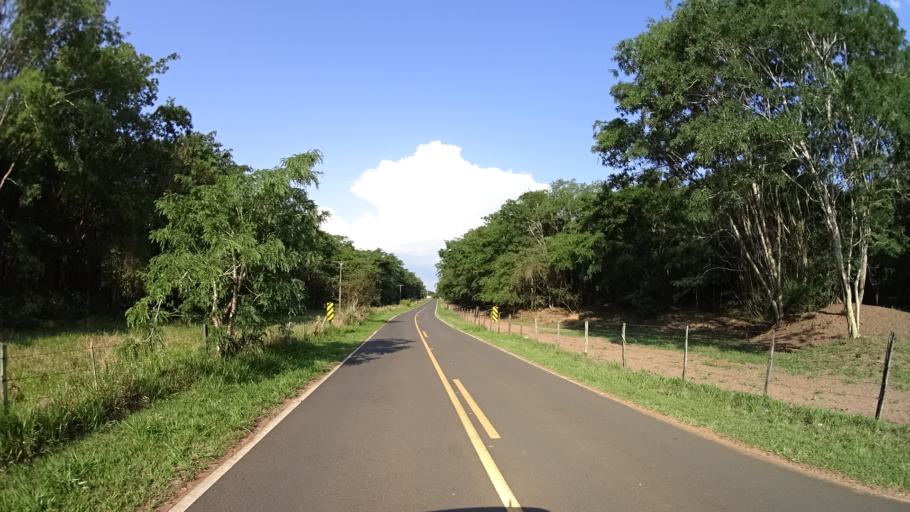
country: BR
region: Sao Paulo
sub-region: Novo Horizonte
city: Novo Horizonte
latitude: -21.4067
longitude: -49.5256
